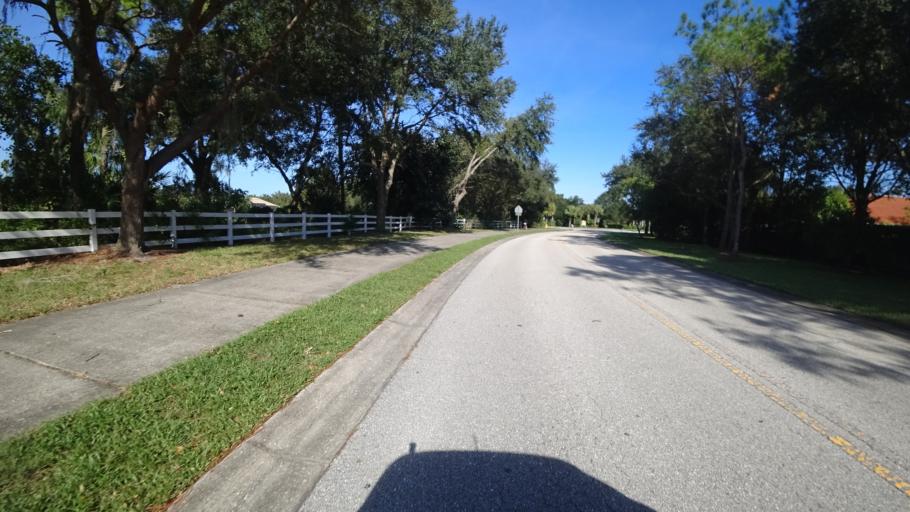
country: US
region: Florida
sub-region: Sarasota County
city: Desoto Lakes
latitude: 27.4328
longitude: -82.4700
